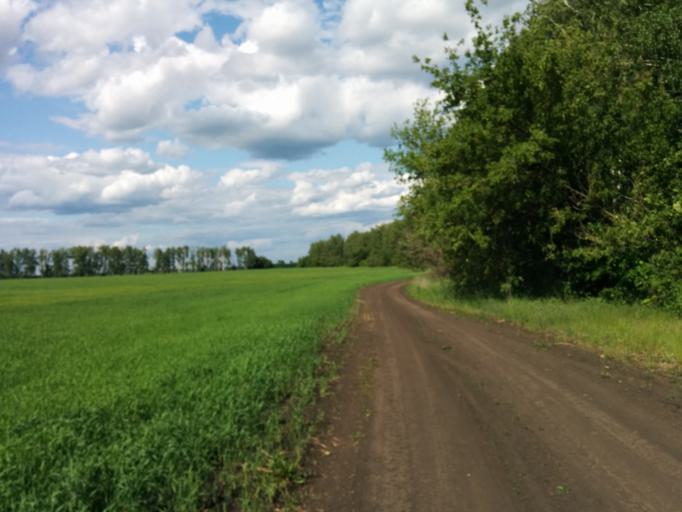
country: RU
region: Tambov
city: Tambov
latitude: 52.8021
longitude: 41.3874
